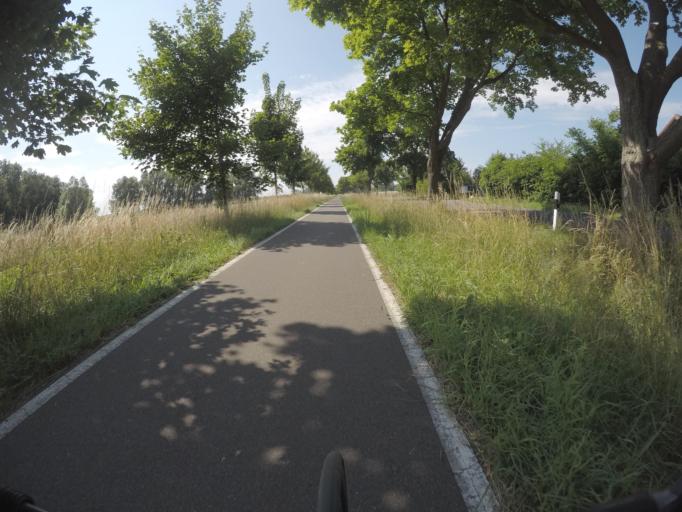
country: DE
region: Mecklenburg-Vorpommern
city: Gingst
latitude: 54.4435
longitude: 13.2112
